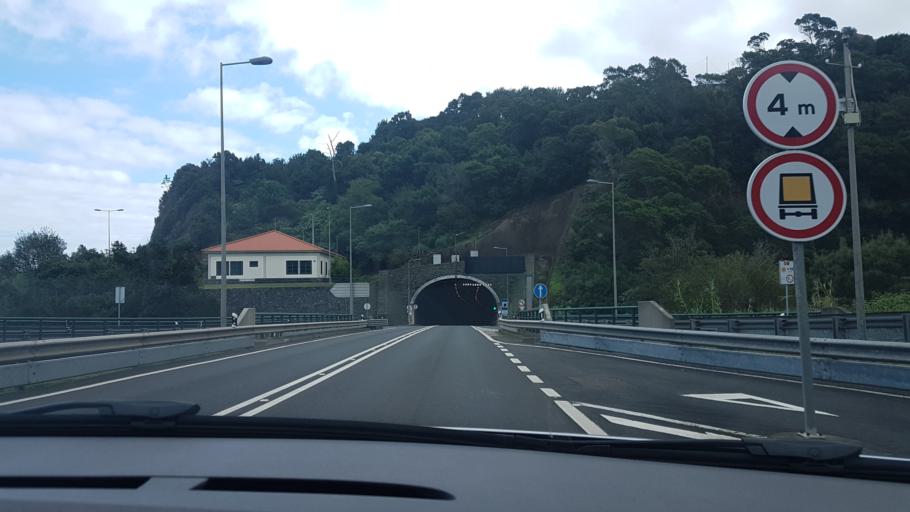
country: PT
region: Madeira
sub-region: Santana
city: Santana
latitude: 32.8093
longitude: -16.8752
